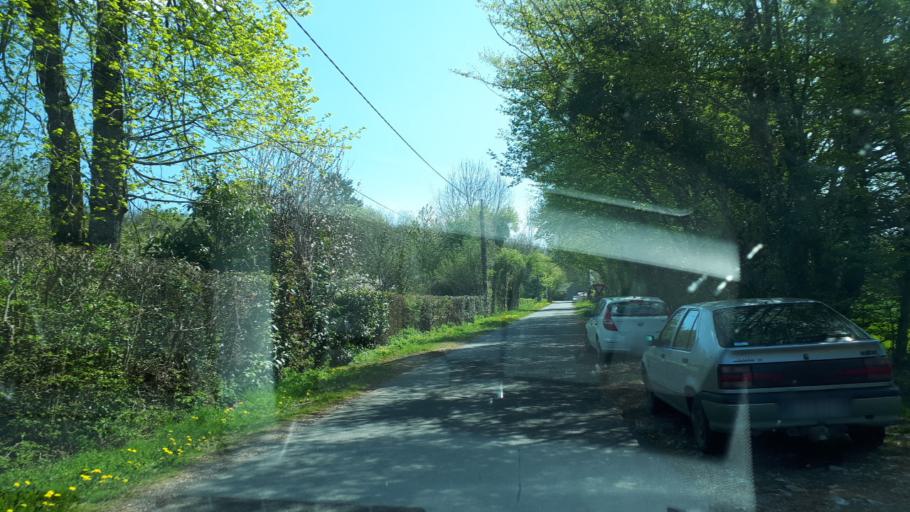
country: FR
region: Centre
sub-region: Departement du Cher
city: Henrichemont
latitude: 47.2986
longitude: 2.5779
